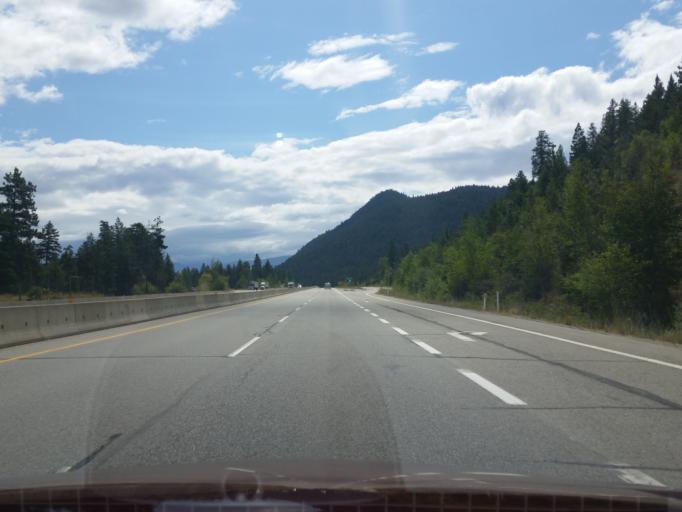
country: CA
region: British Columbia
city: Peachland
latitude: 49.8247
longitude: -119.7909
